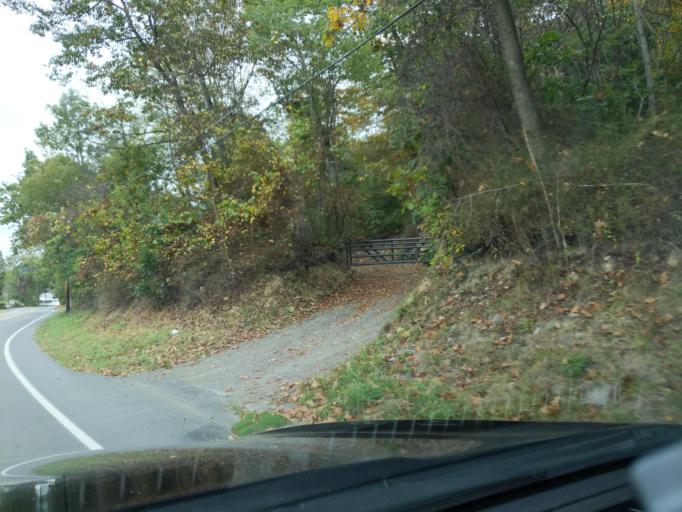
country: US
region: Pennsylvania
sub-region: Blair County
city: Altoona
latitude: 40.4911
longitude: -78.4457
